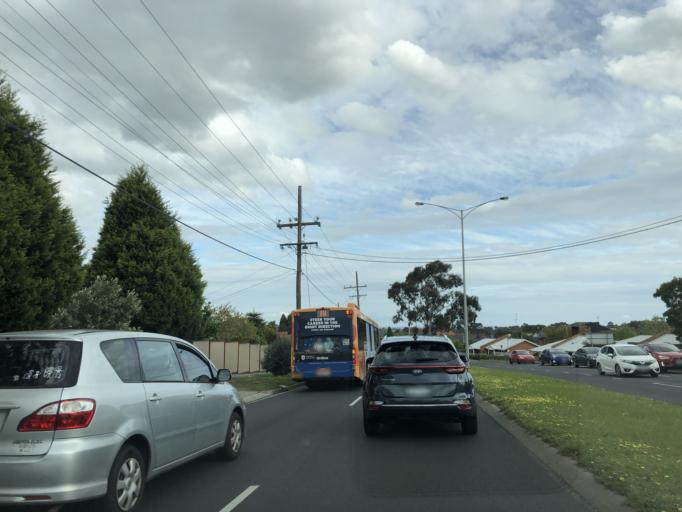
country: AU
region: Victoria
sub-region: Greater Dandenong
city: Noble Park North
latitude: -37.9379
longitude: 145.1925
